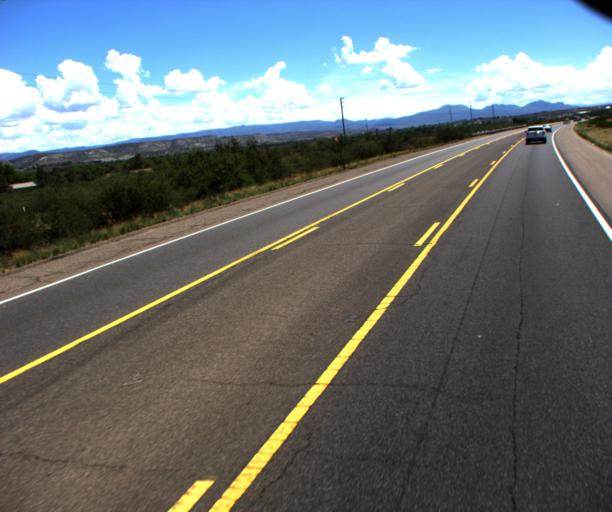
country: US
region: Arizona
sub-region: Yavapai County
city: Camp Verde
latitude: 34.5933
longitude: -111.8904
